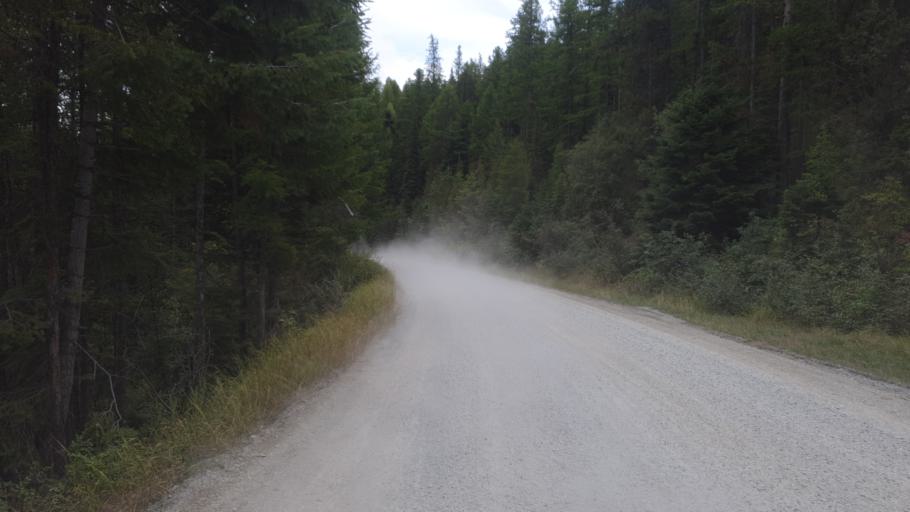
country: US
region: Montana
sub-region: Flathead County
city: Lakeside
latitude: 47.9924
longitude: -114.3266
